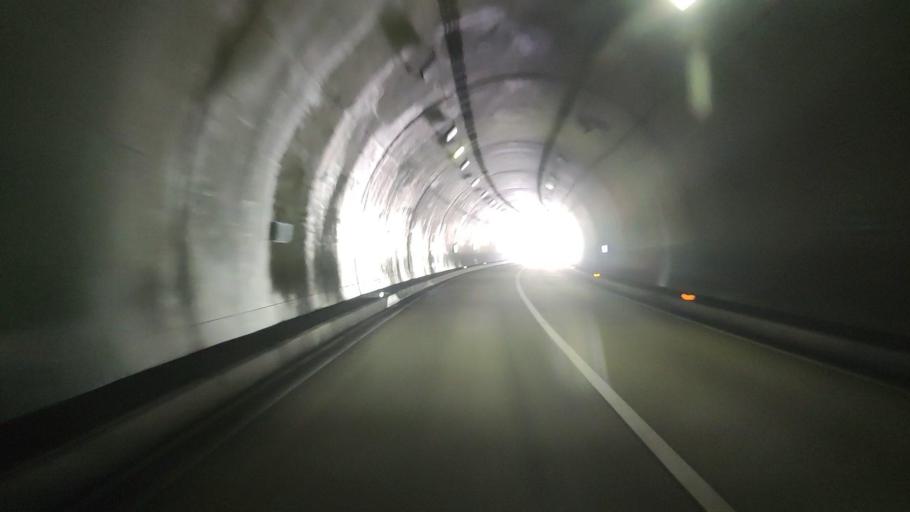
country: JP
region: Wakayama
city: Shingu
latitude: 33.8594
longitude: 135.8520
